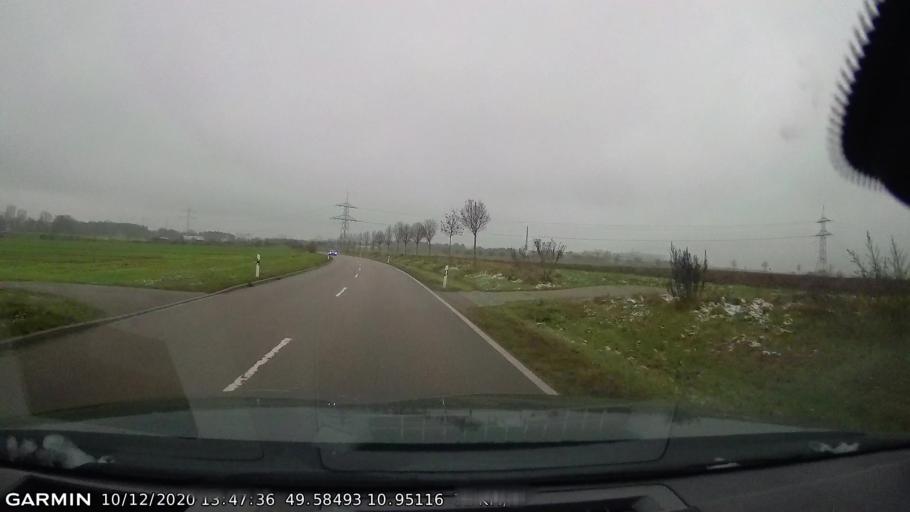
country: DE
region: Bavaria
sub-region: Regierungsbezirk Mittelfranken
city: Erlangen
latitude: 49.5849
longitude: 10.9514
